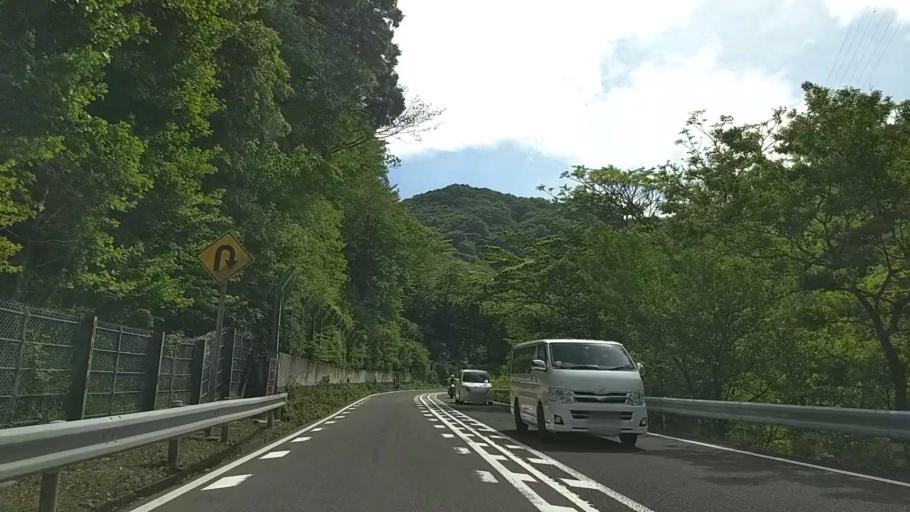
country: JP
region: Kanagawa
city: Hakone
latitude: 35.2098
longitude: 139.0634
